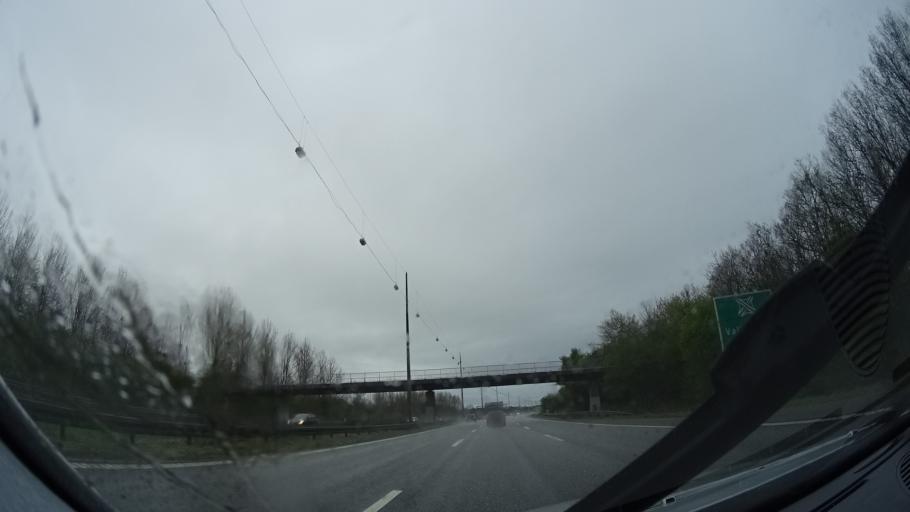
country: DK
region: Capital Region
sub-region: Hoje-Taastrup Kommune
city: Taastrup
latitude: 55.6541
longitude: 12.3237
